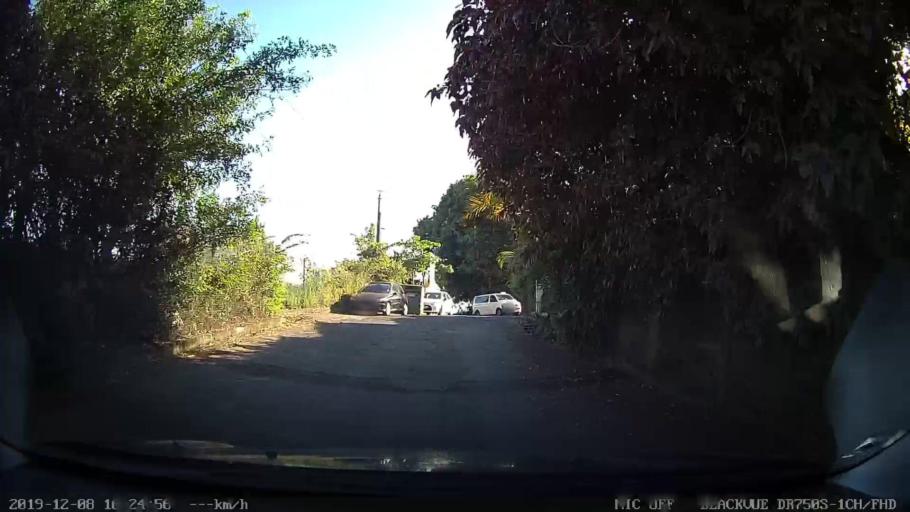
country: RE
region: Reunion
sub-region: Reunion
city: Sainte-Marie
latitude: -20.9251
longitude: 55.5316
